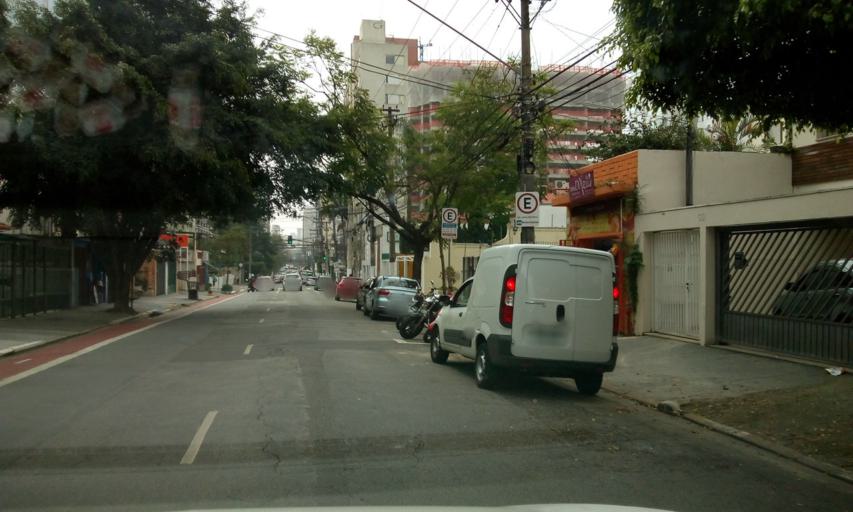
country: BR
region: Sao Paulo
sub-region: Sao Paulo
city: Sao Paulo
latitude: -23.6114
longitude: -46.6621
